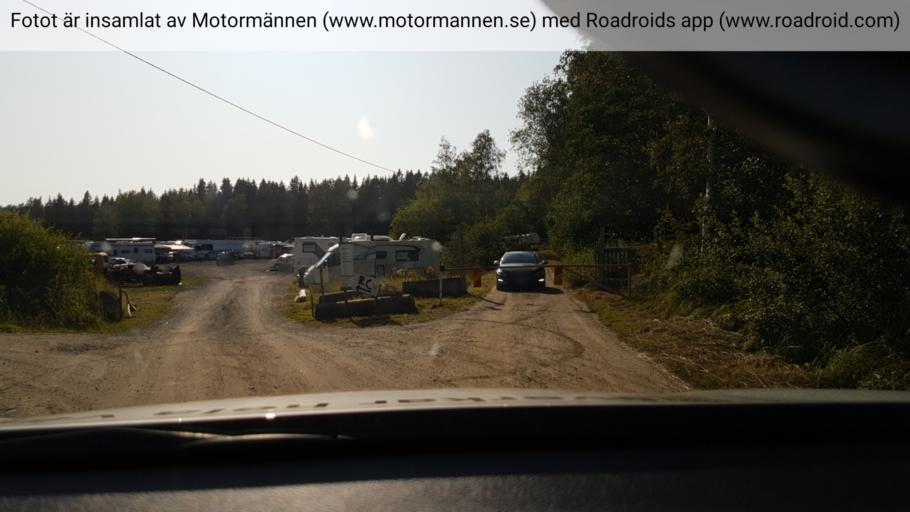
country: SE
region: Stockholm
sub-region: Nynashamns Kommun
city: Osmo
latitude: 58.9356
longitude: 17.9106
